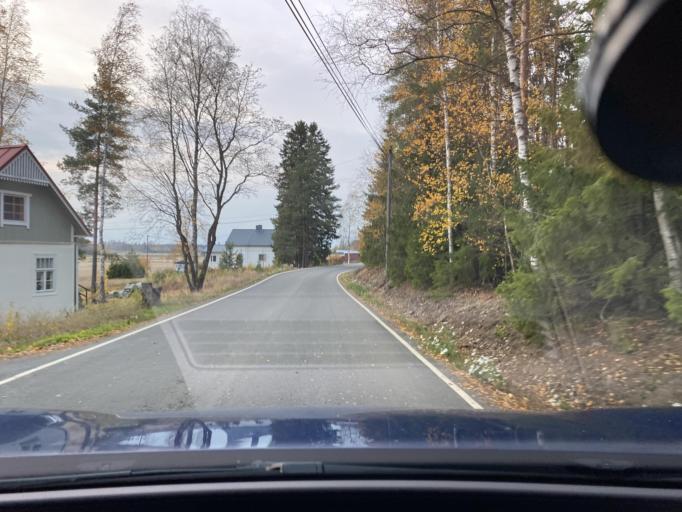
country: FI
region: Varsinais-Suomi
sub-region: Loimaa
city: Alastaro
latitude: 61.0951
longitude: 22.9021
